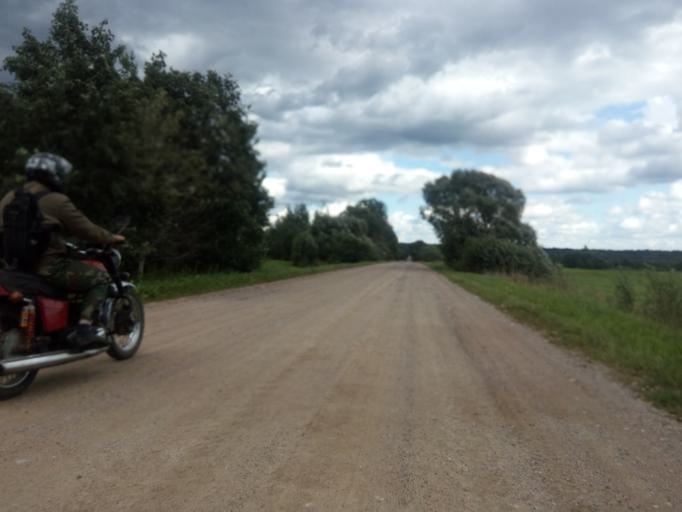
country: BY
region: Vitebsk
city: Dzisna
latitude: 55.7089
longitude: 28.3071
